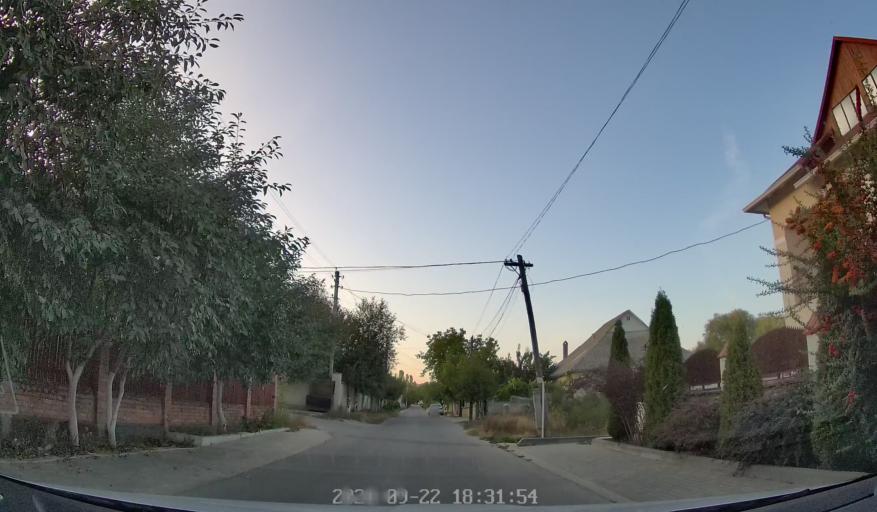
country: MD
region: Laloveni
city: Ialoveni
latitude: 46.9602
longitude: 28.7589
